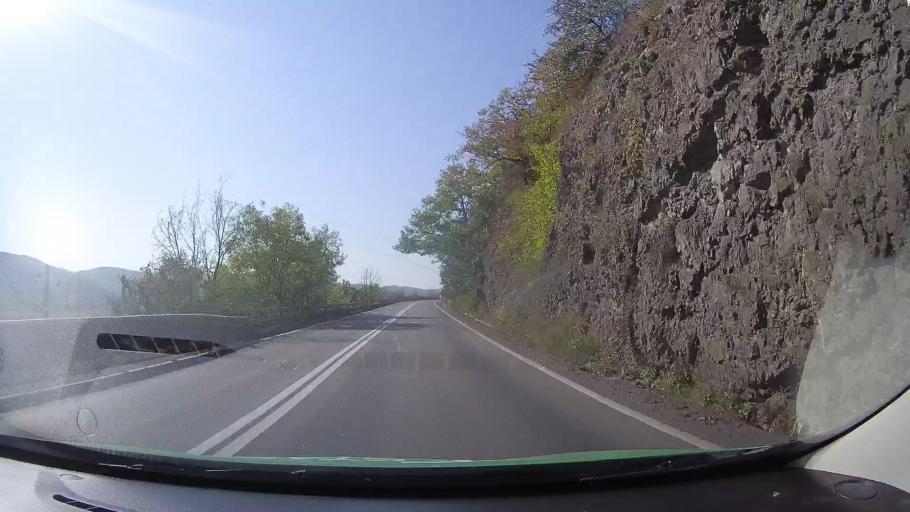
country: RO
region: Arad
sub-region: Comuna Savarsin
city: Savarsin
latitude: 46.0007
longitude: 22.3114
